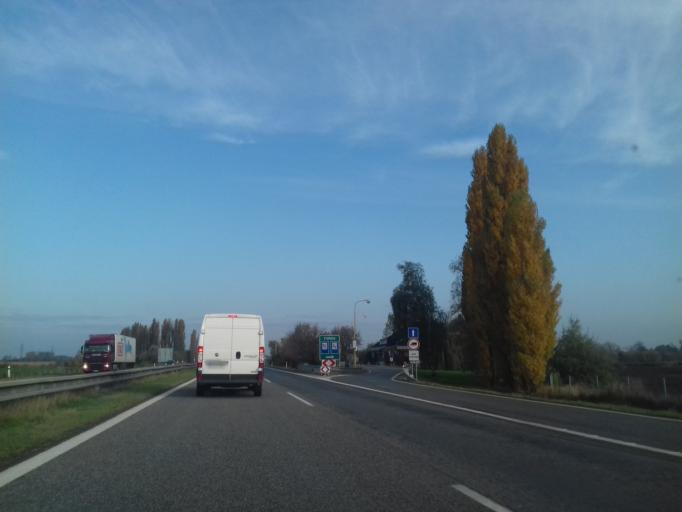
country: SK
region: Bratislavsky
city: Stupava
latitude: 48.2583
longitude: 17.0104
